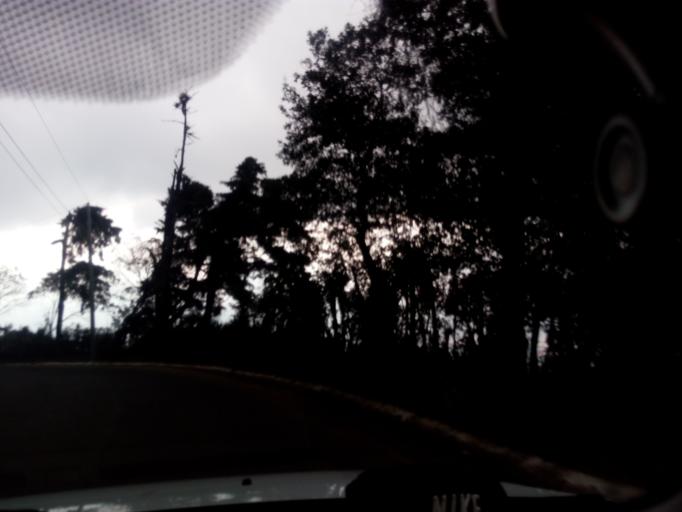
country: GT
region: Sacatepequez
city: Antigua Guatemala
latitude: 14.5776
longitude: -90.7175
